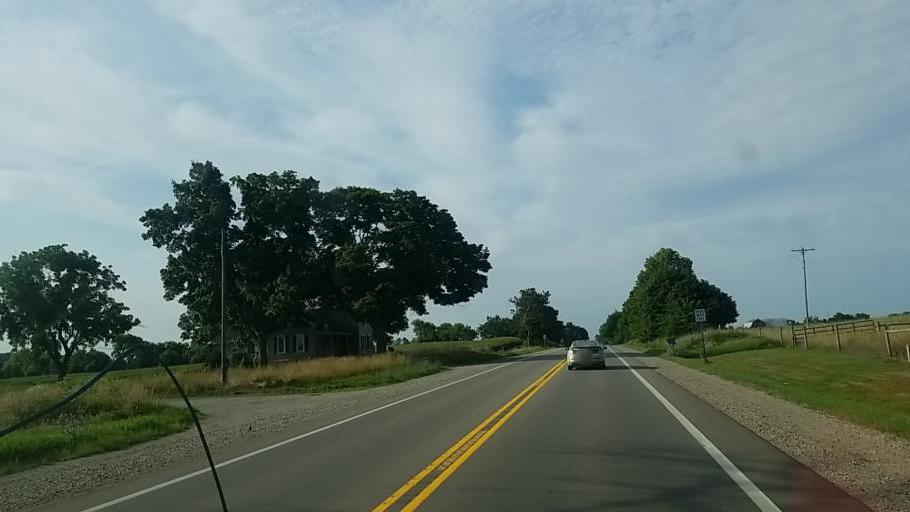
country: US
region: Michigan
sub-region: Ionia County
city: Ionia
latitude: 42.9100
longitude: -85.0749
